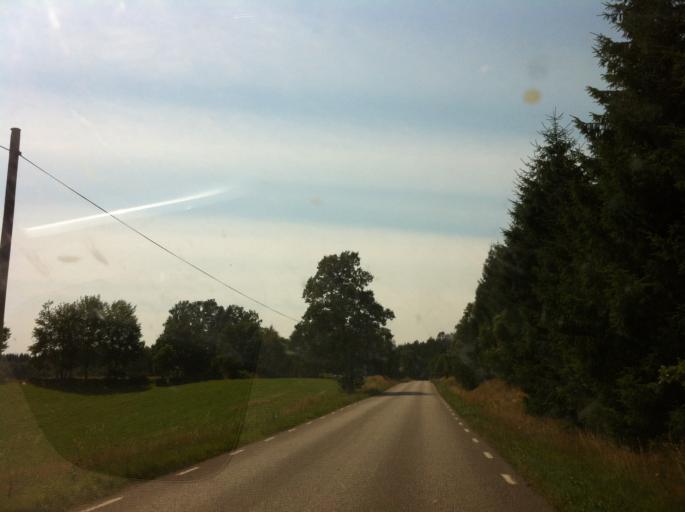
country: SE
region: Skane
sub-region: Hoors Kommun
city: Hoeoer
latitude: 56.0007
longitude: 13.4849
